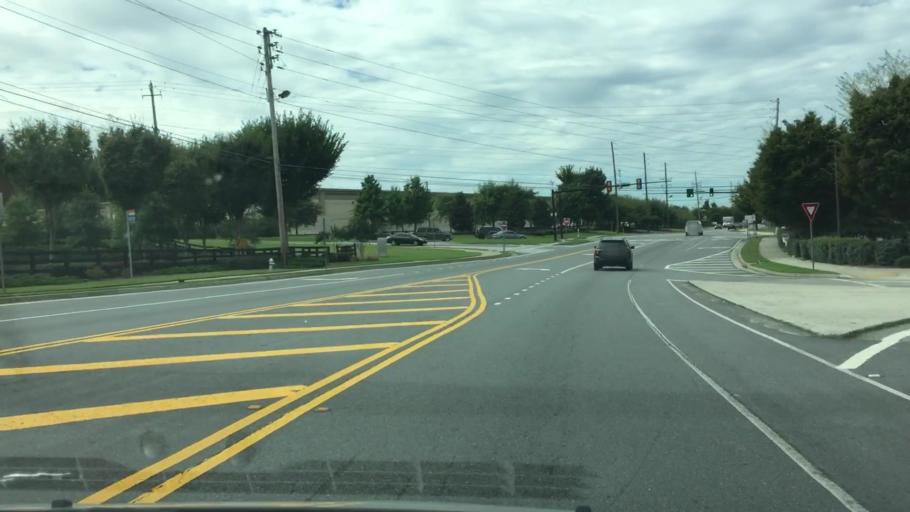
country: US
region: Georgia
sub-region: Fulton County
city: Alpharetta
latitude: 34.0990
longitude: -84.2712
